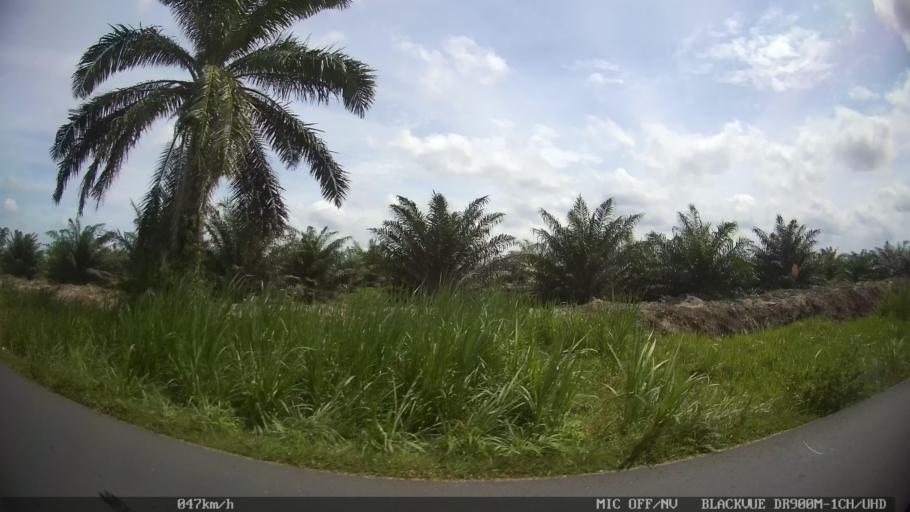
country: ID
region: North Sumatra
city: Percut
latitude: 3.5891
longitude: 98.8745
